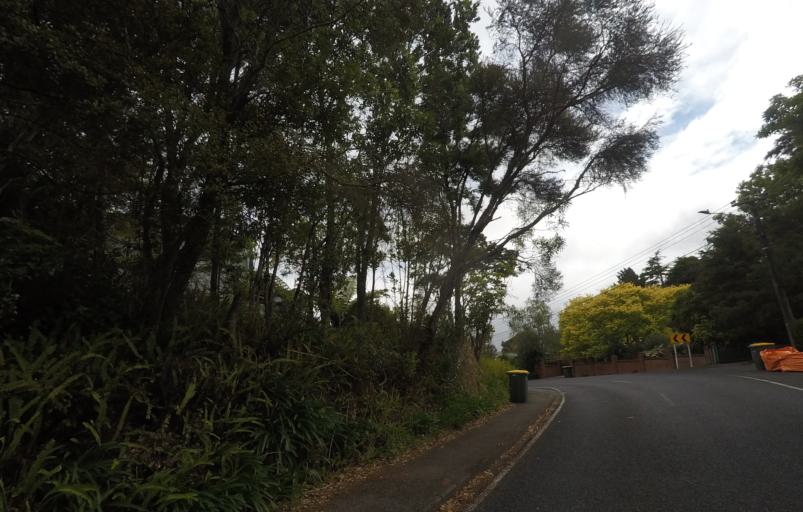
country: NZ
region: Auckland
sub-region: Auckland
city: Titirangi
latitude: -36.9381
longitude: 174.6691
